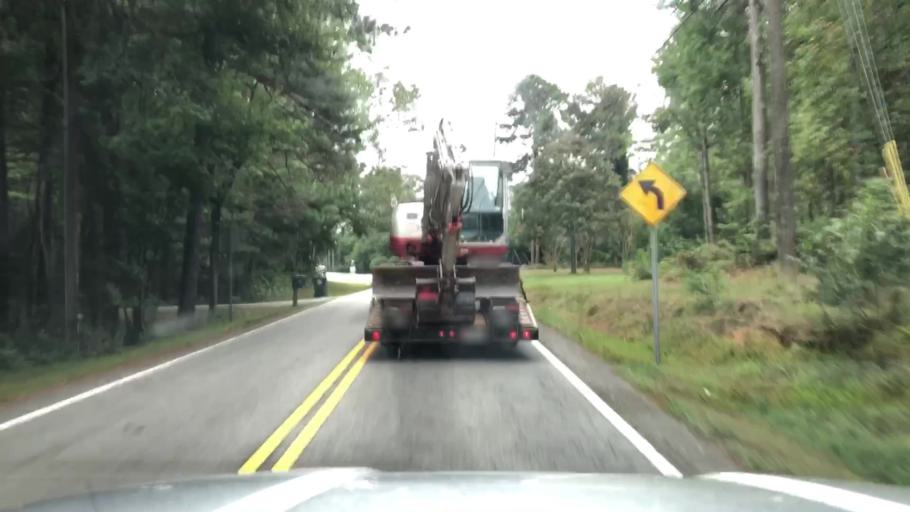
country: US
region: Georgia
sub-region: Bartow County
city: Emerson
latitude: 34.0403
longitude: -84.7737
